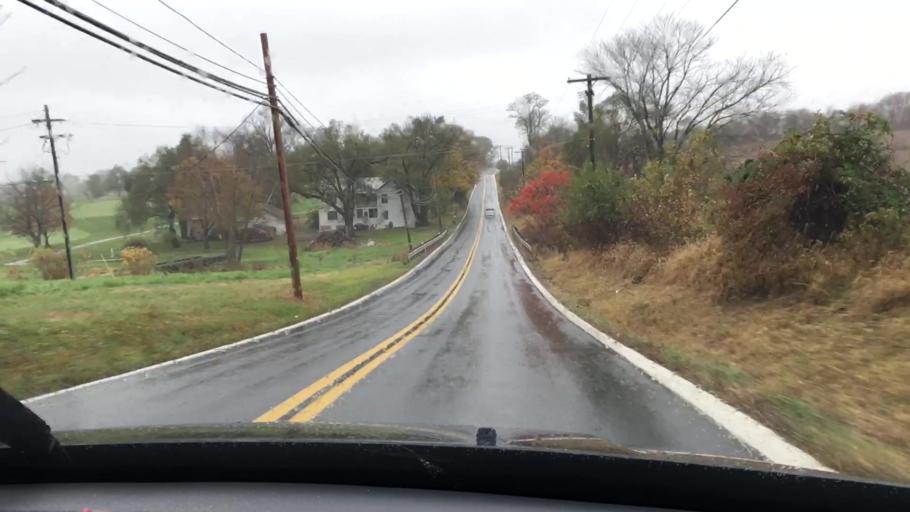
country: US
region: Maryland
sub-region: Frederick County
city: Urbana
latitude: 39.3291
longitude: -77.3770
